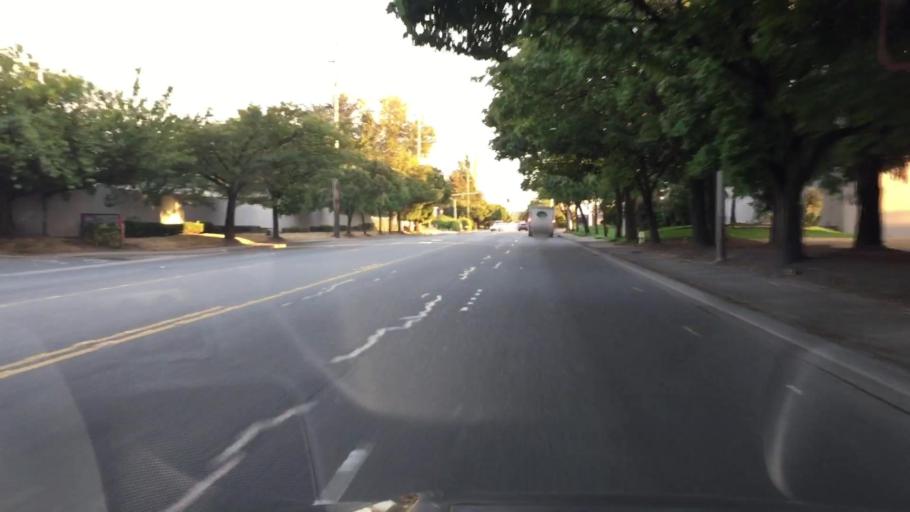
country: US
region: Washington
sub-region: King County
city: Kent
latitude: 47.4276
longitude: -122.2281
